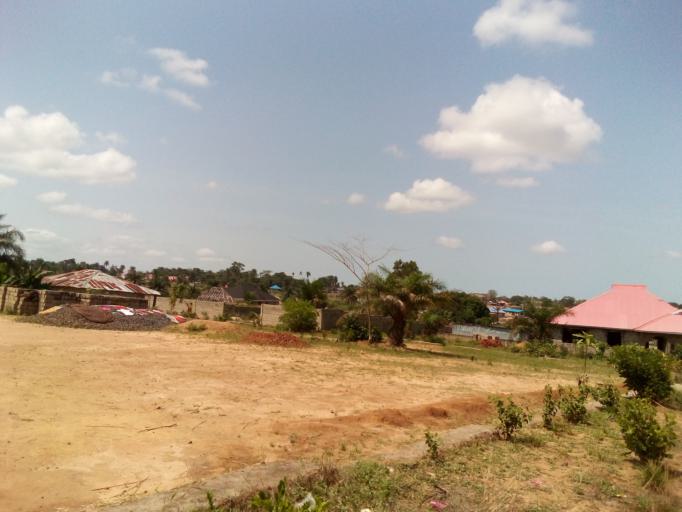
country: SL
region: Western Area
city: Waterloo
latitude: 8.3436
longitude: -13.0197
